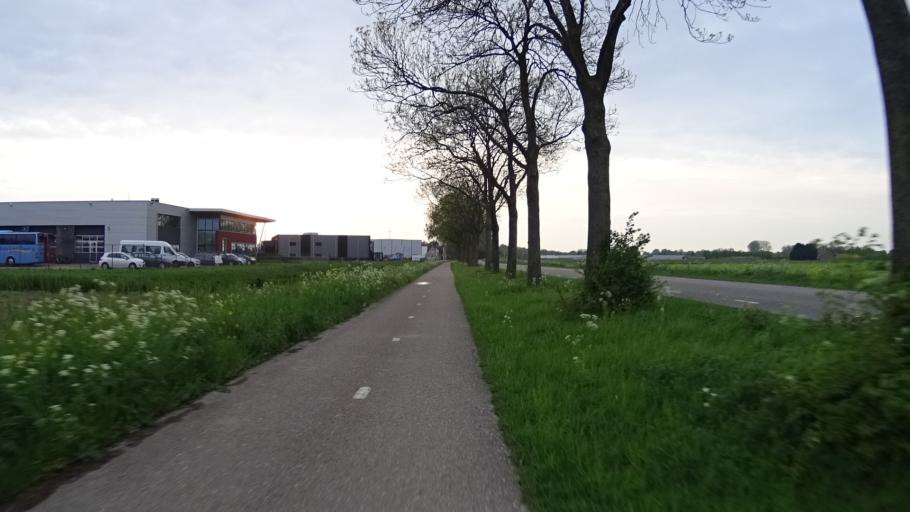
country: NL
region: North Brabant
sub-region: Gemeente Woudrichem
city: Woudrichem
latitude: 51.7810
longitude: 5.0423
